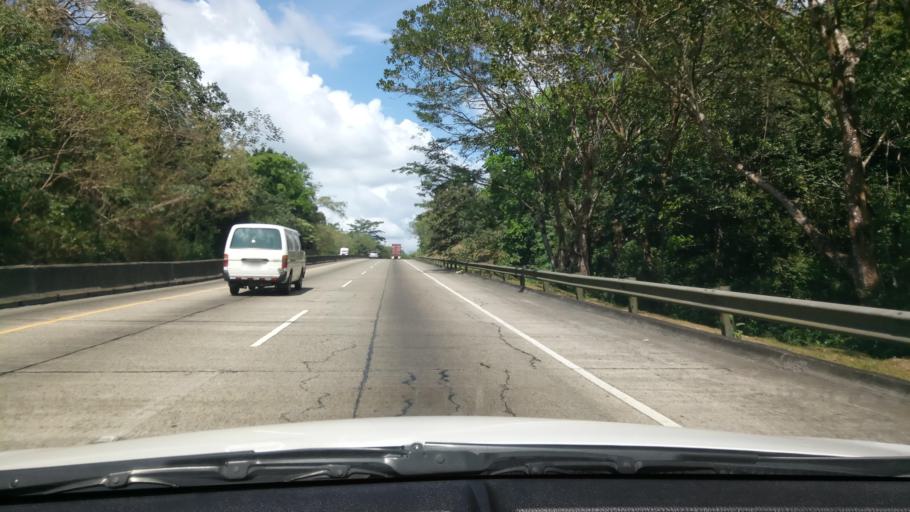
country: PA
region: Panama
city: Alcalde Diaz
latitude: 9.0874
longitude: -79.6002
